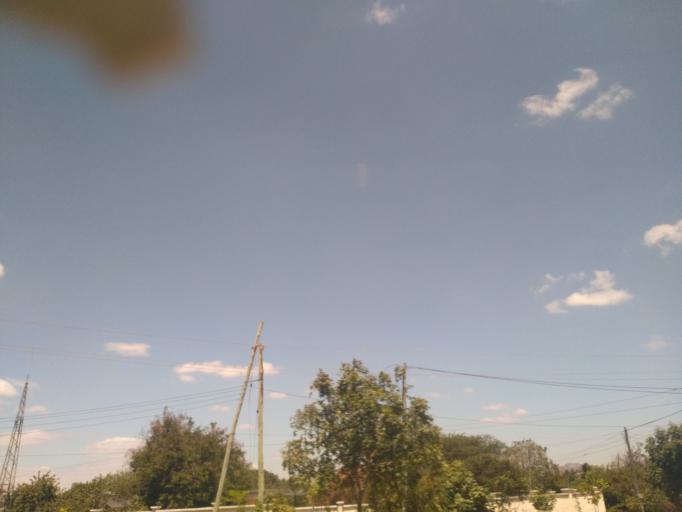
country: TZ
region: Dodoma
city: Dodoma
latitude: -6.1813
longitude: 35.7330
